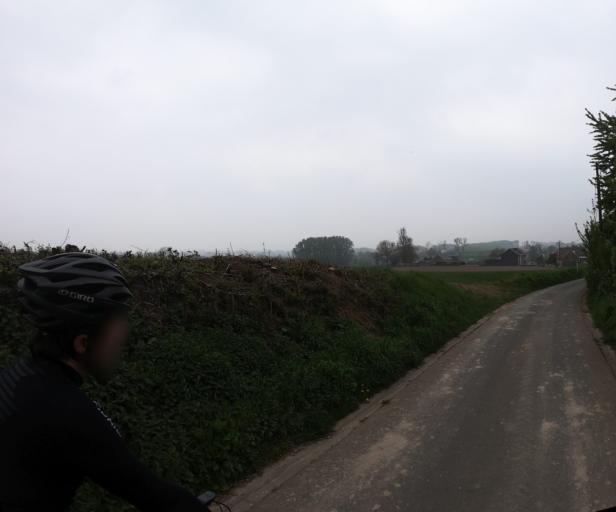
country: BE
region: Flanders
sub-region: Provincie Vlaams-Brabant
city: Pepingen
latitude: 50.7305
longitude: 4.1568
